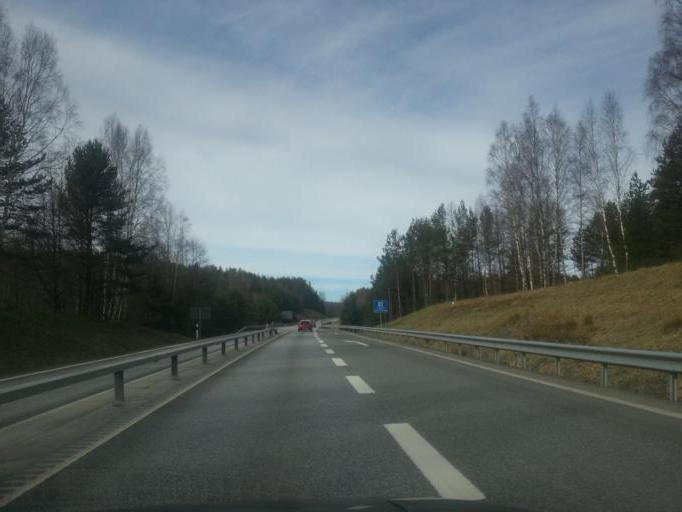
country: SE
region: Joenkoeping
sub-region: Jonkopings Kommun
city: Bankeryd
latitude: 57.8670
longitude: 14.1034
